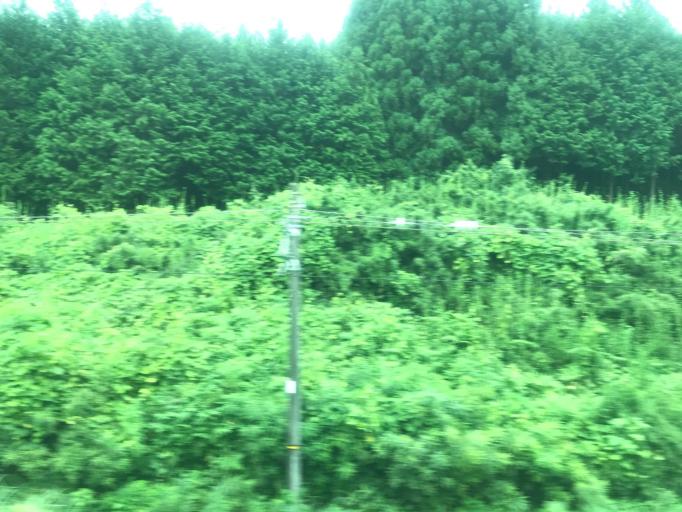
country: JP
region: Fukushima
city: Nihommatsu
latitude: 37.6239
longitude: 140.4719
